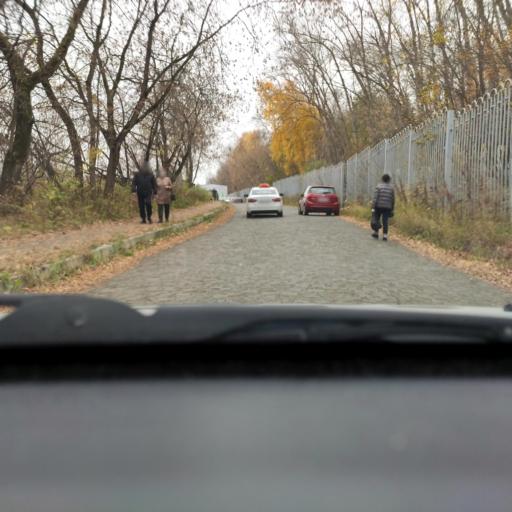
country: RU
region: Perm
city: Perm
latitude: 57.9951
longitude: 56.2788
